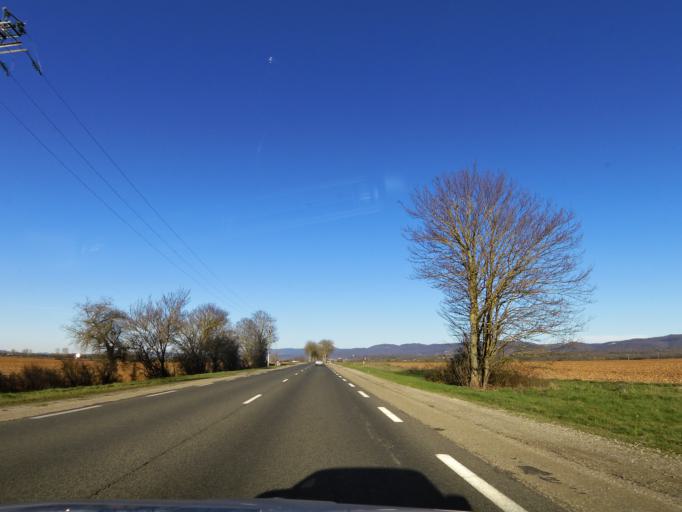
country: FR
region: Rhone-Alpes
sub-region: Departement de l'Ain
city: Chazey-sur-Ain
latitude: 45.9136
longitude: 5.2540
